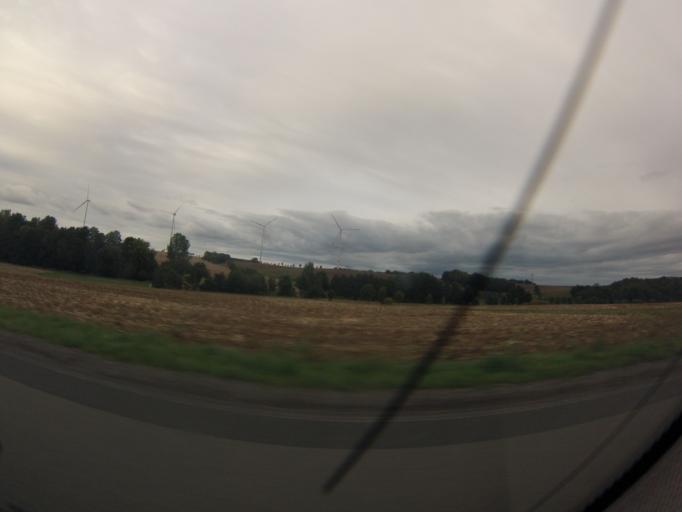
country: DE
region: Thuringia
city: Wildenborten
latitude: 50.8970
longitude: 12.2947
